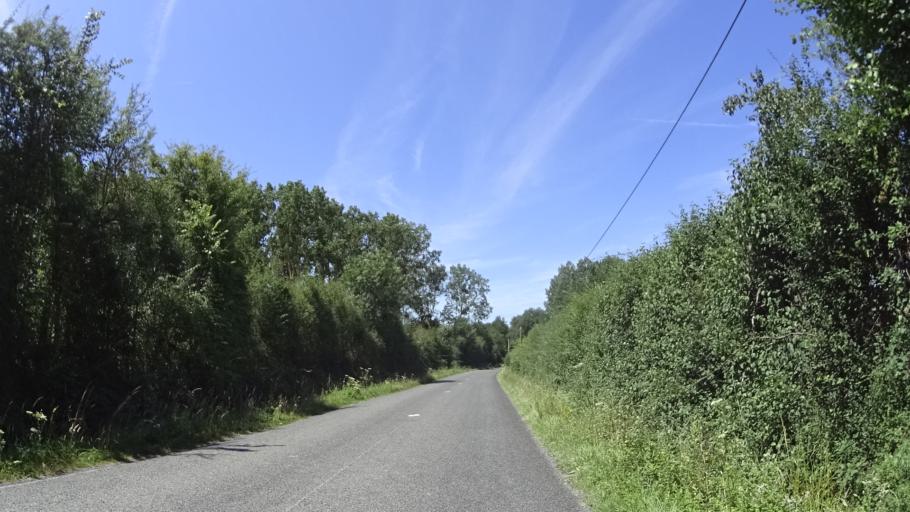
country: FR
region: Pays de la Loire
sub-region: Departement de Maine-et-Loire
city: Grez-Neuville
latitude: 47.6306
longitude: -0.7561
